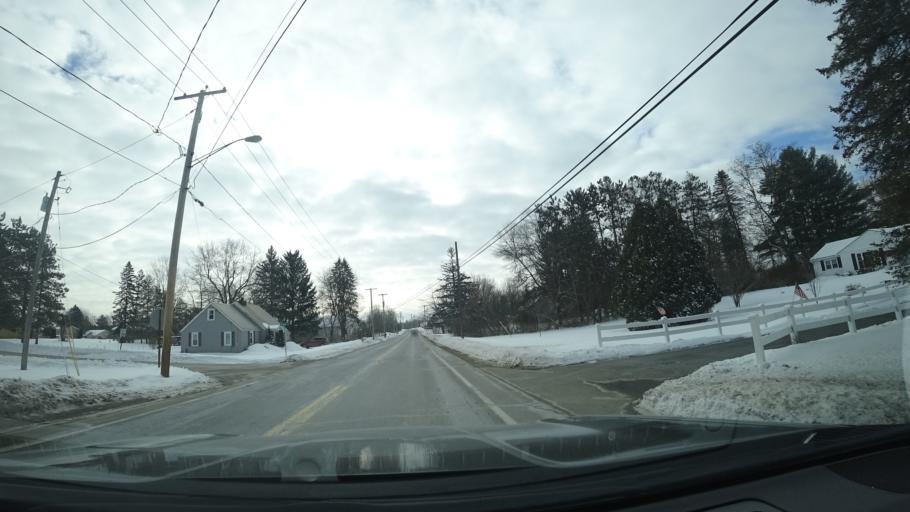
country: US
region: New York
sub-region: Saratoga County
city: South Glens Falls
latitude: 43.2891
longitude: -73.6260
